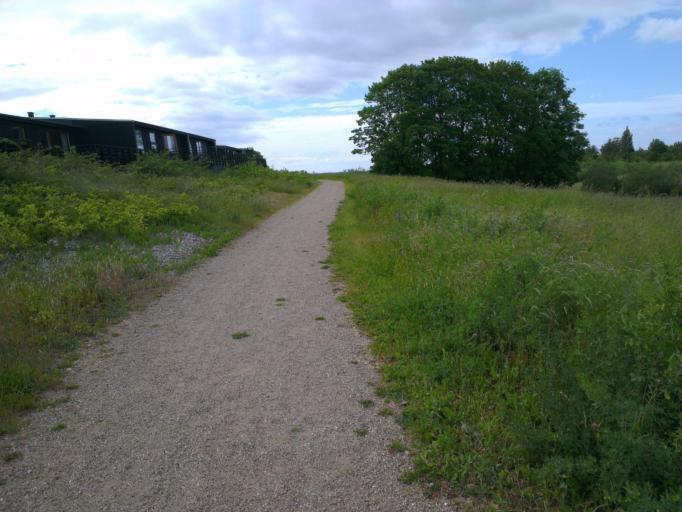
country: DK
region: Capital Region
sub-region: Frederikssund Kommune
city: Frederikssund
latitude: 55.8652
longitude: 12.0767
